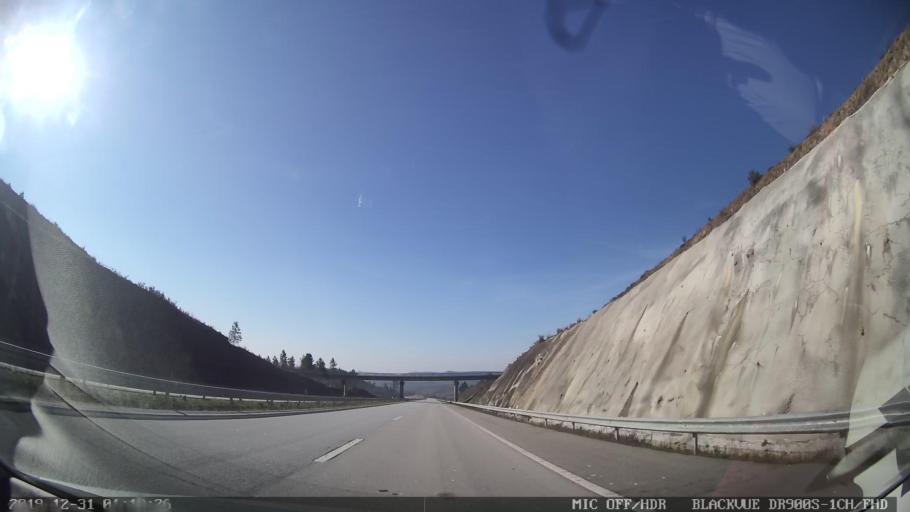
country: PT
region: Portalegre
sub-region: Gaviao
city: Gaviao
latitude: 39.5435
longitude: -7.8827
